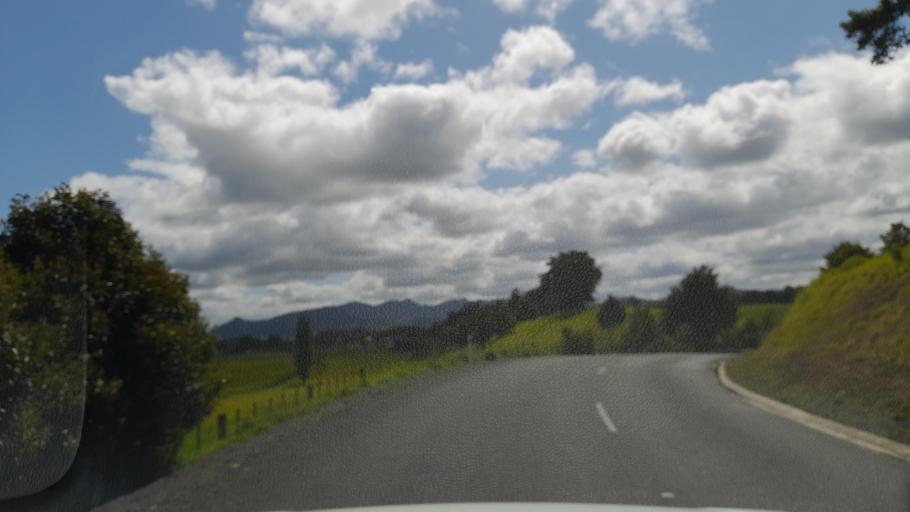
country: NZ
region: Northland
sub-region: Whangarei
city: Maungatapere
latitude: -35.7109
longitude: 174.0516
